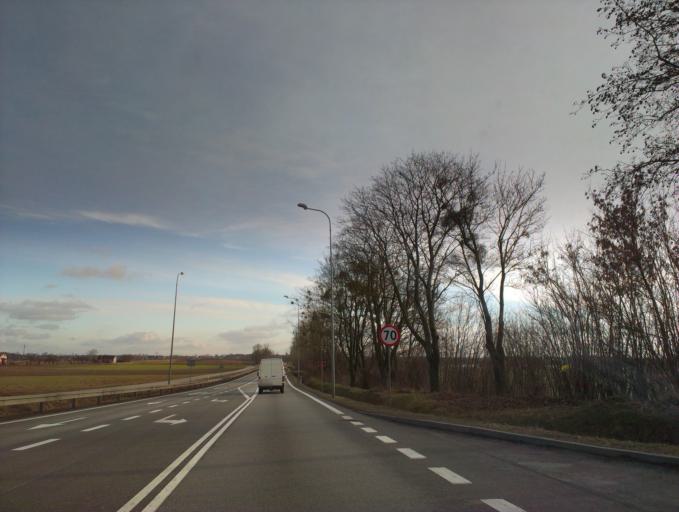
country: PL
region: Kujawsko-Pomorskie
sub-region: Powiat lipnowski
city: Kikol
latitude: 52.9260
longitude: 19.0850
